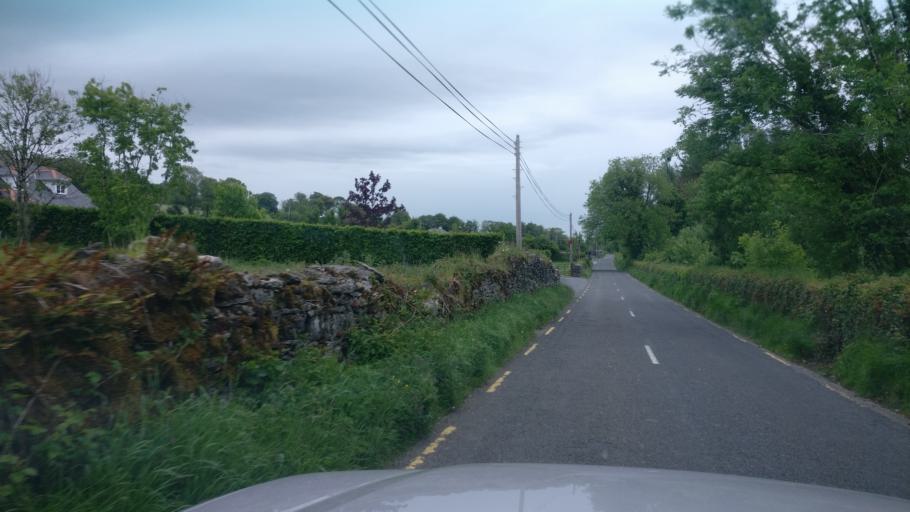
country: IE
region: Connaught
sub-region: County Galway
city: Loughrea
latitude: 53.0896
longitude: -8.4775
